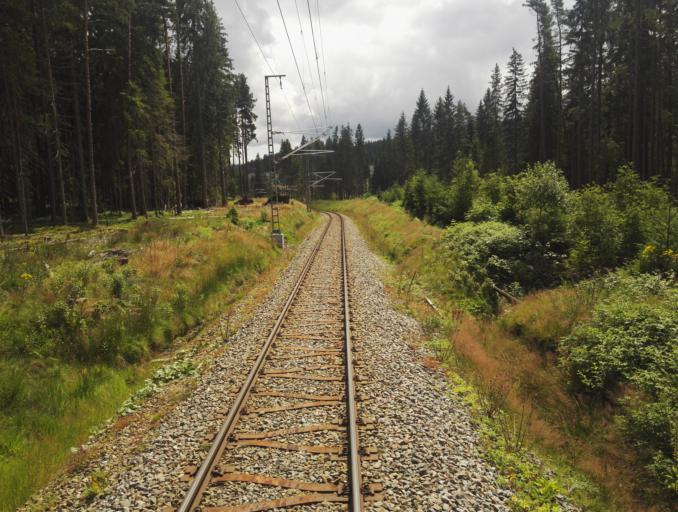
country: DE
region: Baden-Wuerttemberg
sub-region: Freiburg Region
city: Hinterzarten
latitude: 47.8631
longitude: 8.1064
